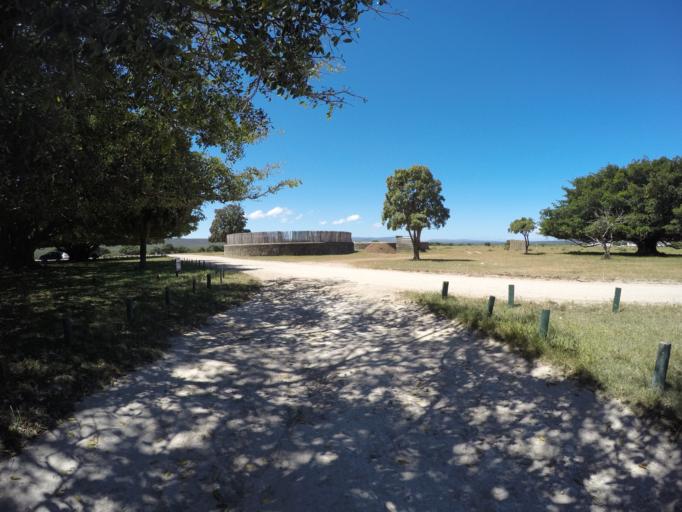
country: ZA
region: Western Cape
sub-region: Overberg District Municipality
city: Bredasdorp
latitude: -34.4547
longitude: 20.3996
